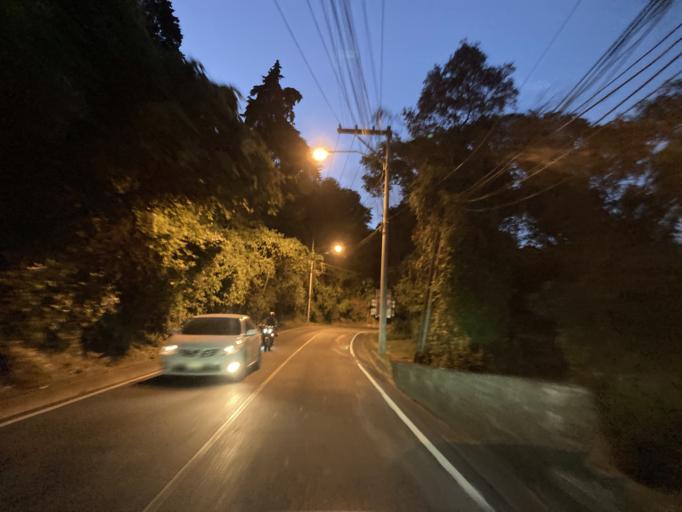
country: GT
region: Guatemala
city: Santa Catarina Pinula
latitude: 14.5945
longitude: -90.4640
